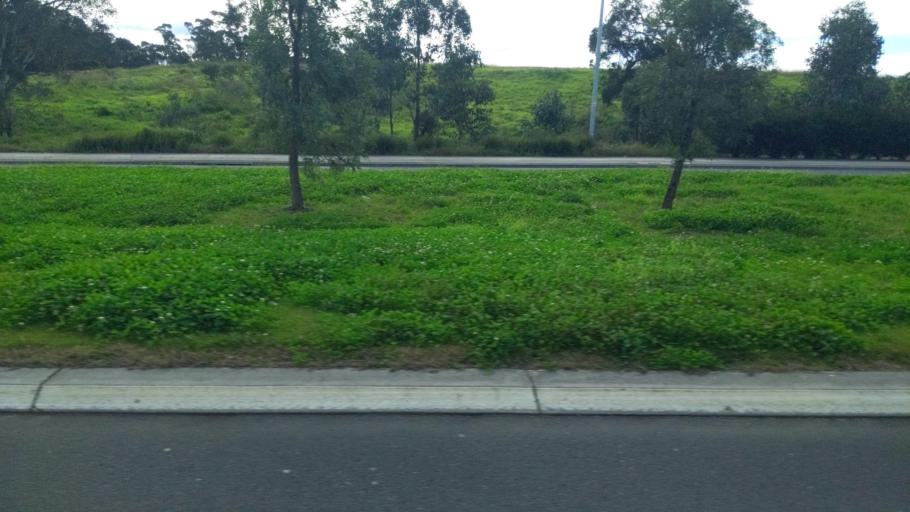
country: AU
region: New South Wales
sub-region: Blacktown
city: Riverstone
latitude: -33.7051
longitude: 150.8510
